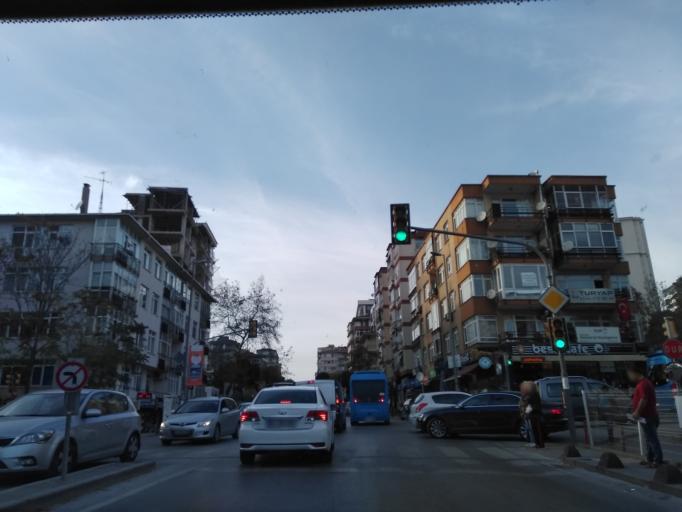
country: TR
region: Istanbul
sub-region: Atasehir
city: Atasehir
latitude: 40.9573
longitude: 29.0975
